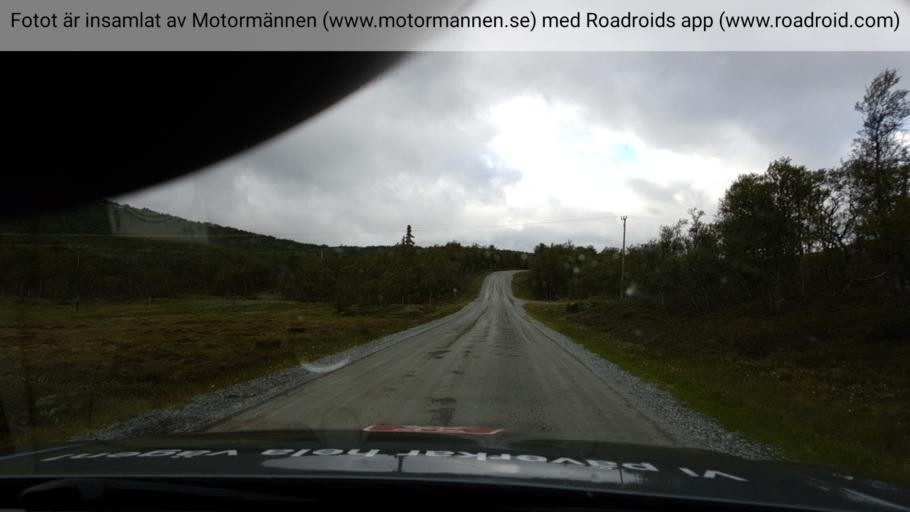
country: SE
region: Jaemtland
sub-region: Are Kommun
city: Are
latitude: 62.8870
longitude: 12.7204
